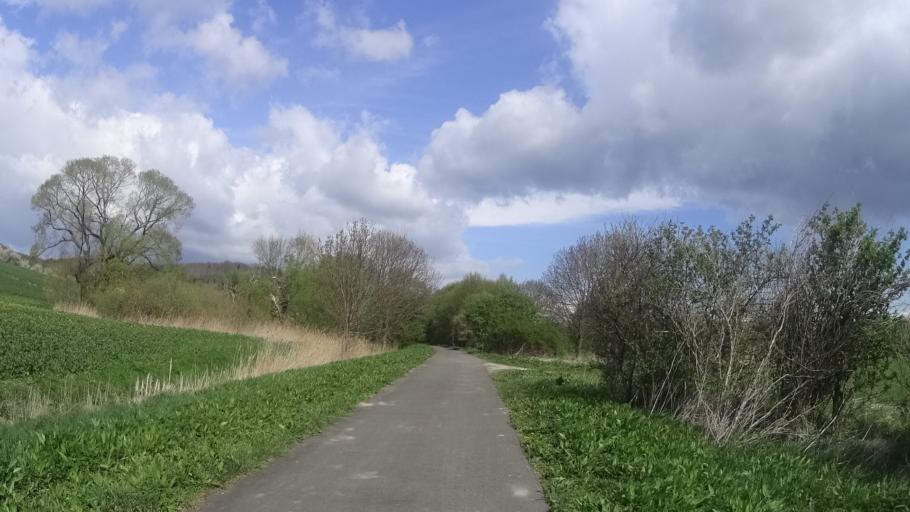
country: DE
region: Thuringia
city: Wandersleben
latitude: 50.8801
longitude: 10.8470
